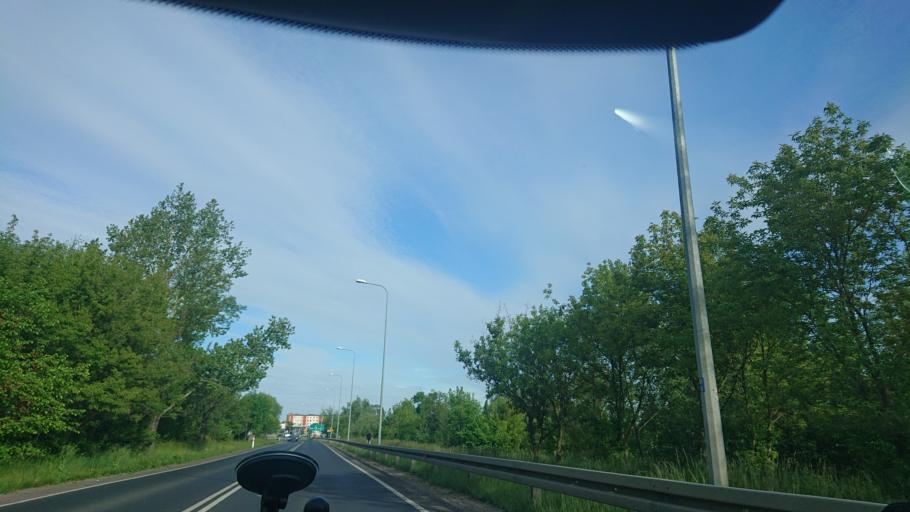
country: PL
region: Greater Poland Voivodeship
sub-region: Powiat gnieznienski
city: Gniezno
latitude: 52.5150
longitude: 17.5891
